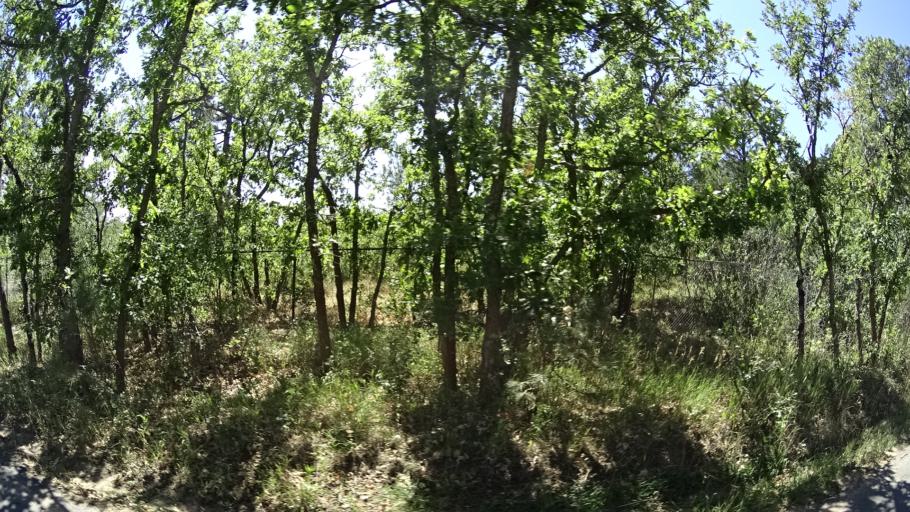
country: US
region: Colorado
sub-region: El Paso County
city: Colorado Springs
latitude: 38.7743
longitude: -104.8476
